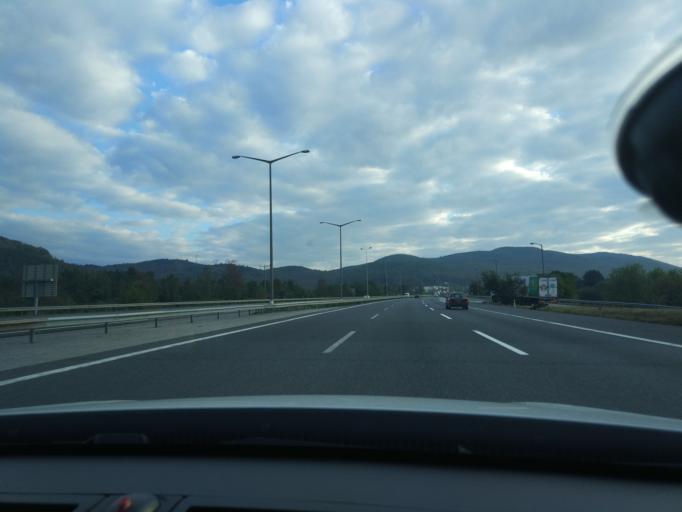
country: TR
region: Sakarya
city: Karadere
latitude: 40.8022
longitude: 30.8501
